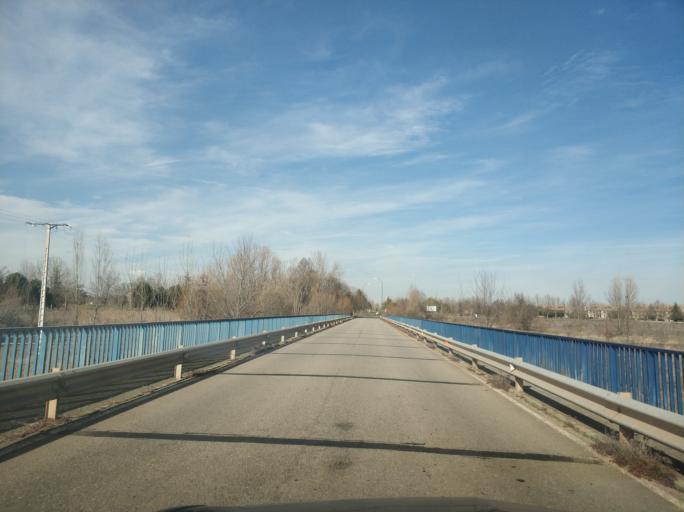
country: ES
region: Castille and Leon
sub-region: Provincia de Salamanca
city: Villamayor
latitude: 40.9921
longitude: -5.7283
